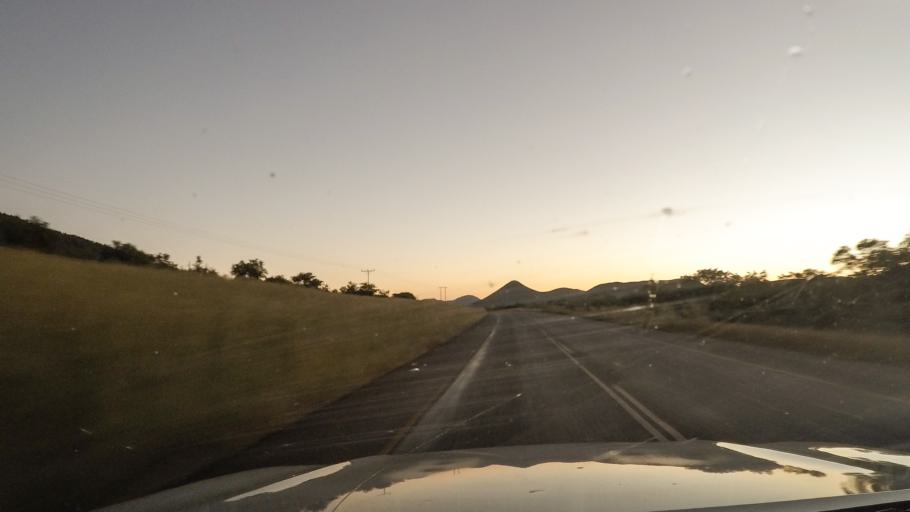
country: BW
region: South East
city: Lobatse
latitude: -25.1296
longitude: 25.7023
